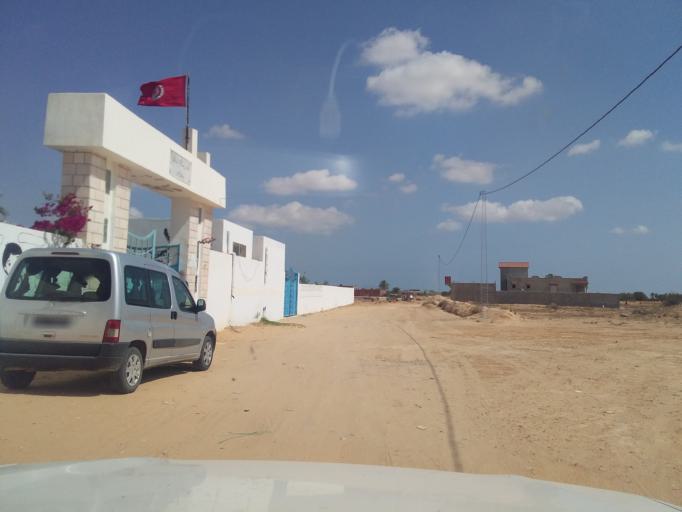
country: TN
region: Madanin
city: Medenine
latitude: 33.6047
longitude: 10.3048
